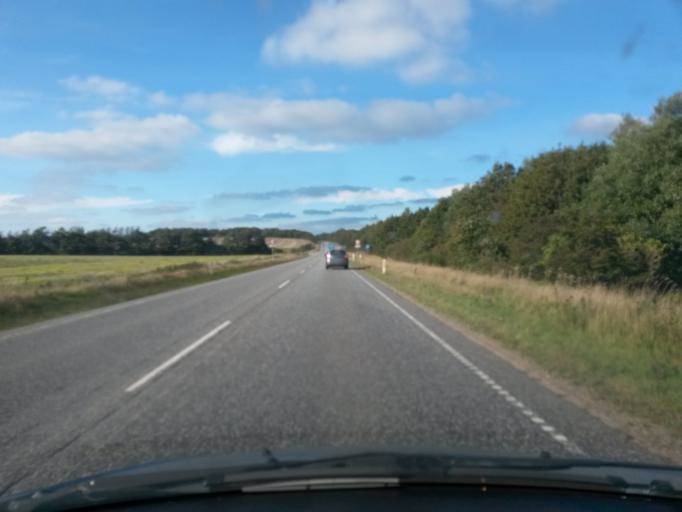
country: DK
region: Central Jutland
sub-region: Herning Kommune
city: Avlum
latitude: 56.2797
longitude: 8.7537
